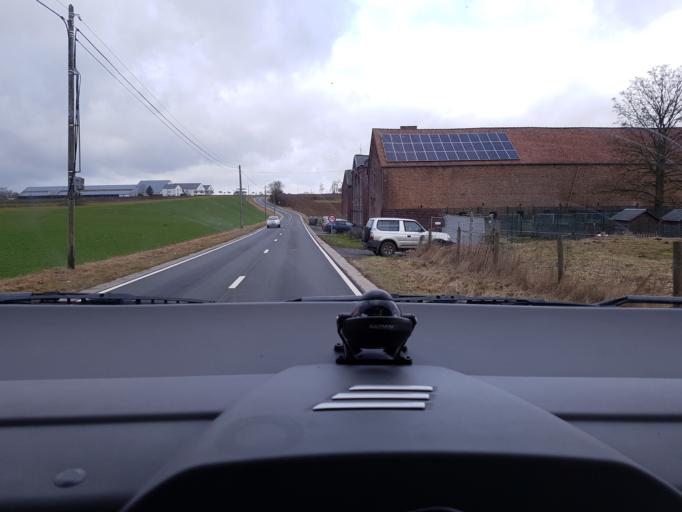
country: BE
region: Wallonia
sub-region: Province de Namur
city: Ciney
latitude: 50.2890
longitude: 5.1196
